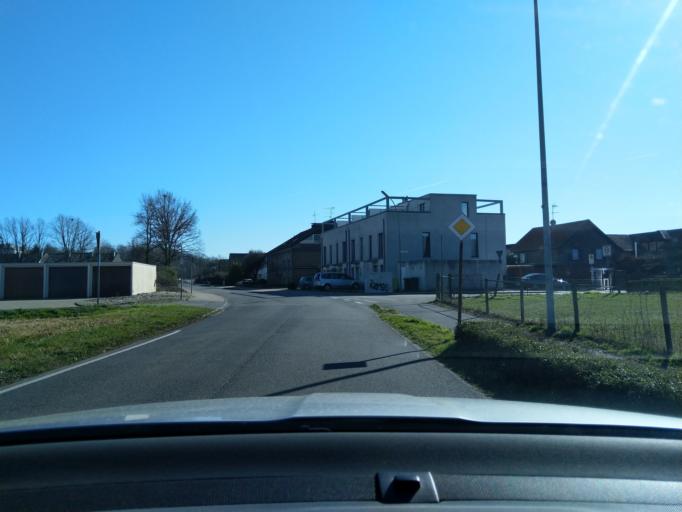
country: DE
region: North Rhine-Westphalia
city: Wegberg
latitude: 51.1416
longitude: 6.2957
